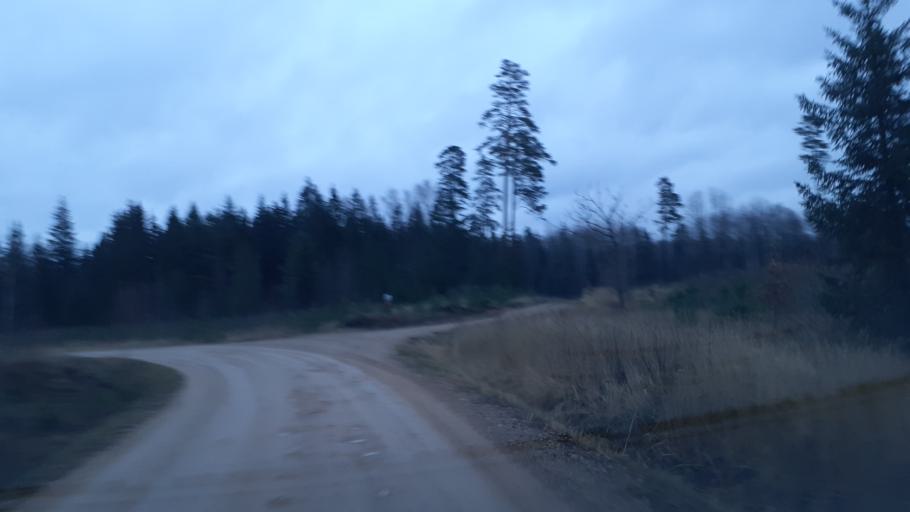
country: LV
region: Kuldigas Rajons
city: Kuldiga
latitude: 56.9945
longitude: 22.0553
